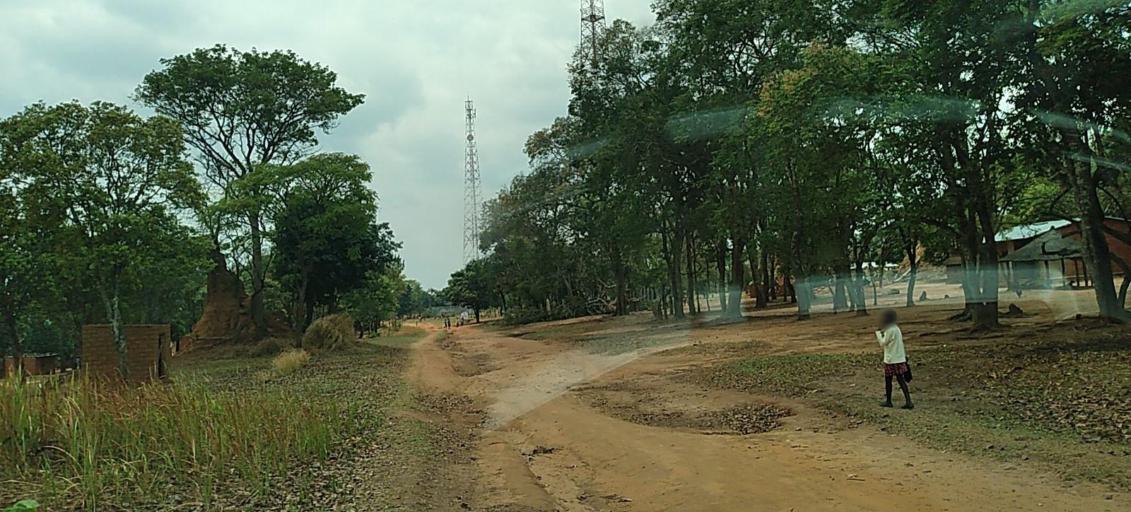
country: ZM
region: North-Western
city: Mwinilunga
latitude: -11.5218
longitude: 24.7884
